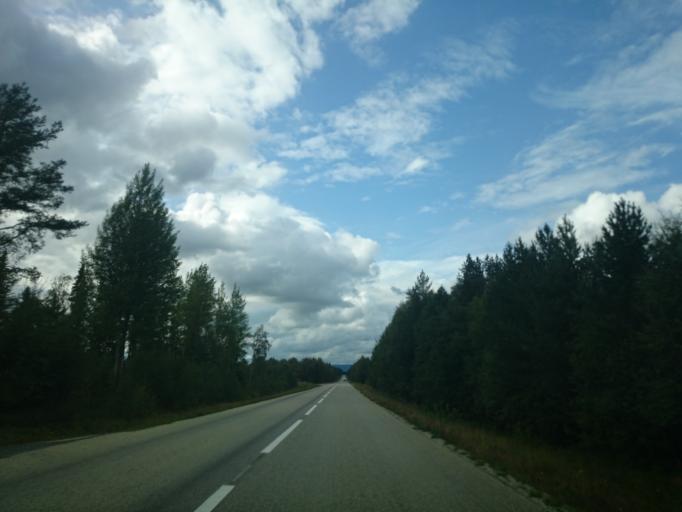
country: SE
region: Jaemtland
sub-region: Harjedalens Kommun
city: Sveg
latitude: 62.4108
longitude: 13.5814
